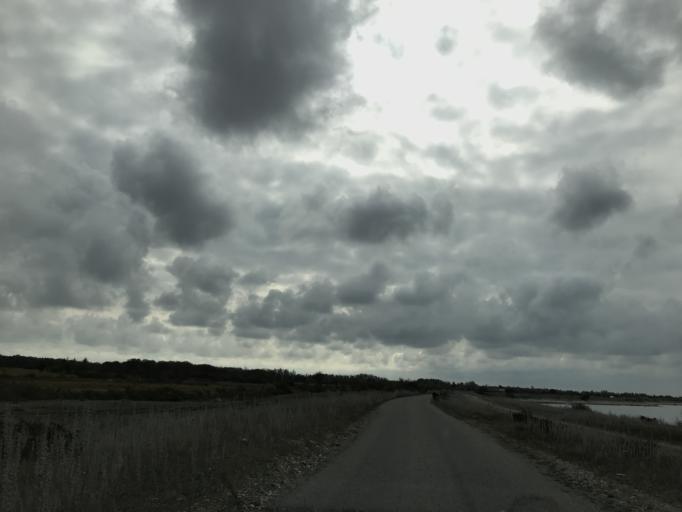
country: SE
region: Kalmar
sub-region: Borgholms Kommun
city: Borgholm
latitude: 57.0530
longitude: 16.8364
